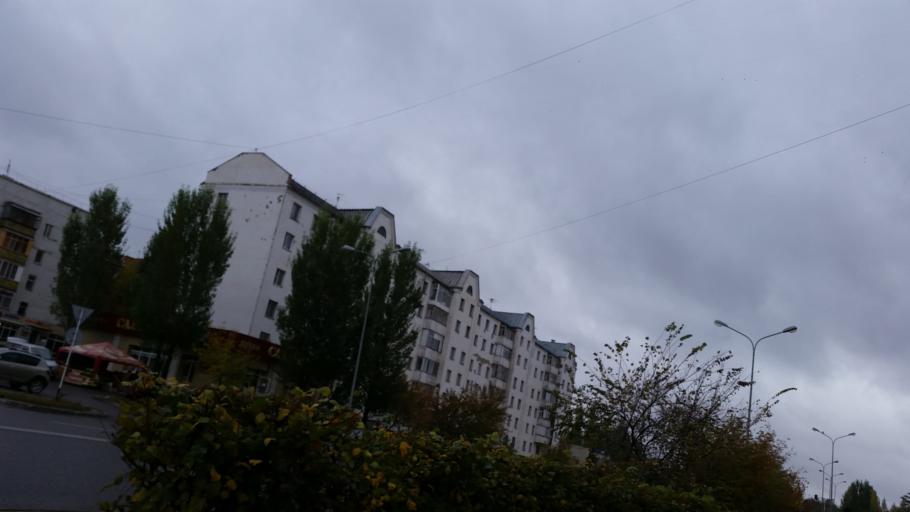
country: KZ
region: Astana Qalasy
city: Astana
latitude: 51.1516
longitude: 71.4998
